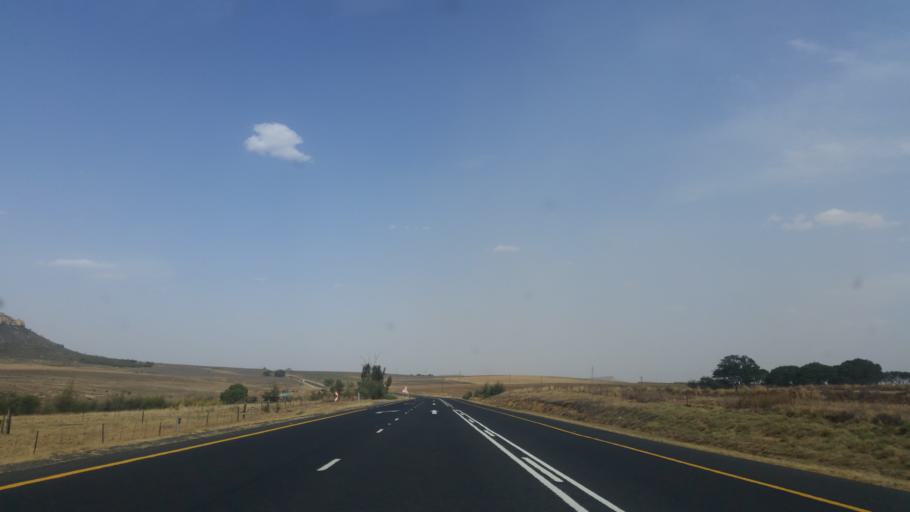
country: ZA
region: Orange Free State
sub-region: Thabo Mofutsanyana District Municipality
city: Bethlehem
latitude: -28.2992
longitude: 28.5442
